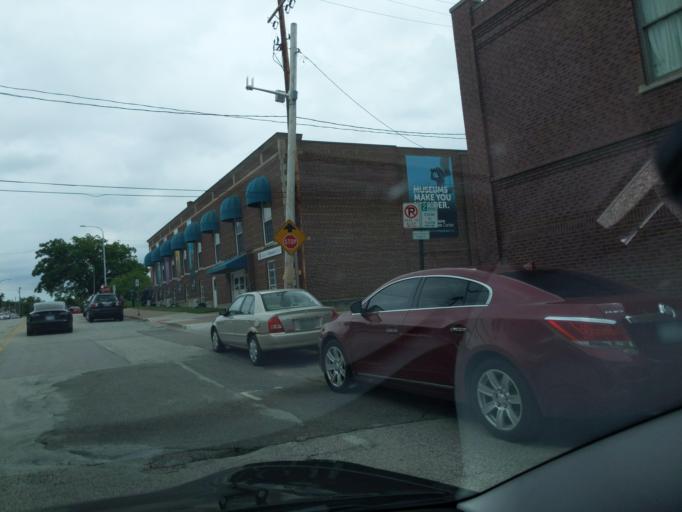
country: US
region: Michigan
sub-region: Muskegon County
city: Muskegon
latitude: 43.2343
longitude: -86.2543
